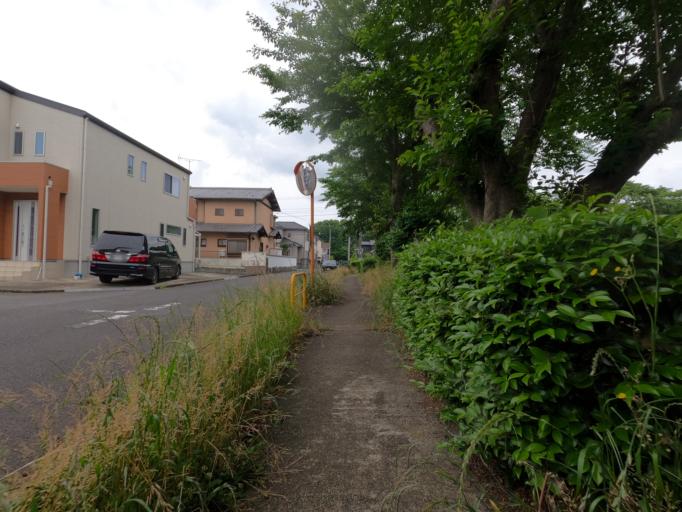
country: JP
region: Ibaraki
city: Moriya
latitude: 35.9576
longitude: 139.9629
